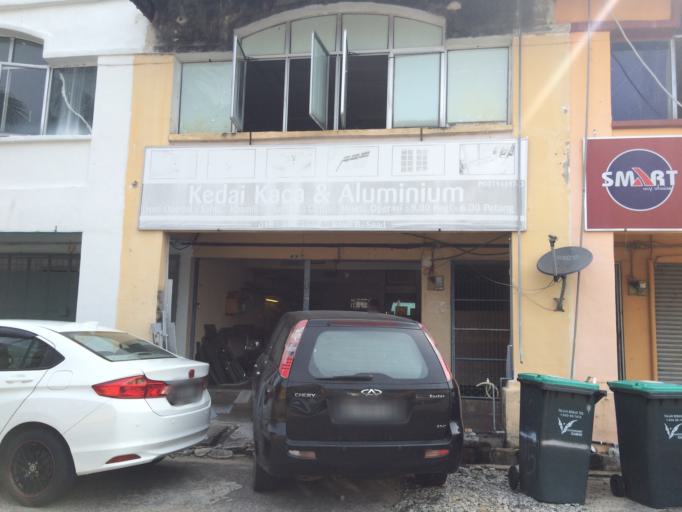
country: MY
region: Kedah
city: Kulim
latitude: 5.3917
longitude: 100.5635
